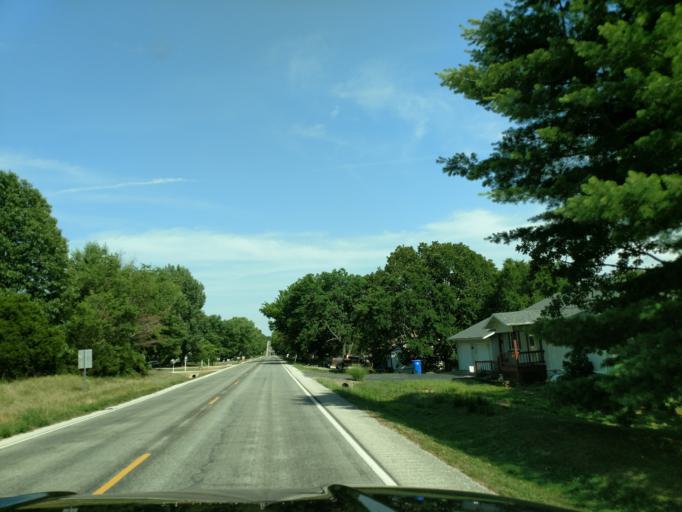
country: US
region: Missouri
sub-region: Barry County
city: Shell Knob
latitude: 36.6169
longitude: -93.6038
